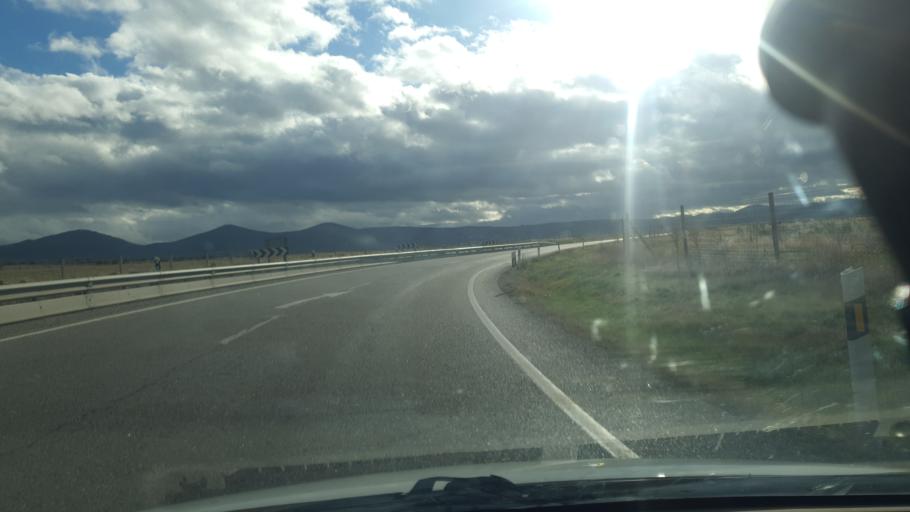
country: ES
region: Castille and Leon
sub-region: Provincia de Segovia
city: Valdeprados
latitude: 40.8275
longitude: -4.2729
